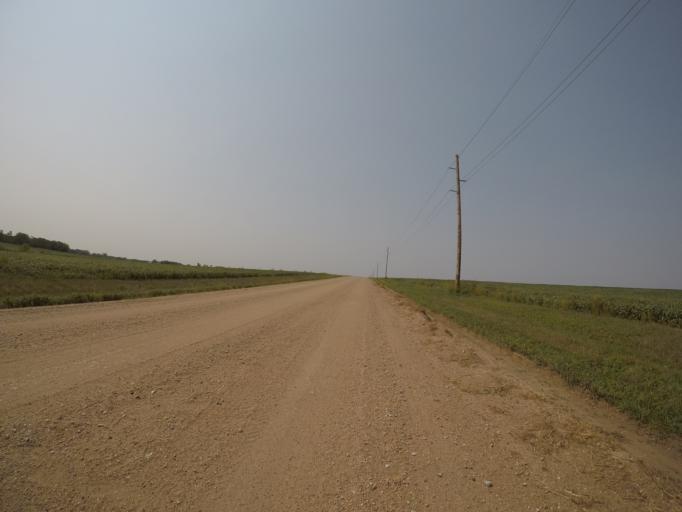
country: US
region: Nebraska
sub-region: Gage County
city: Beatrice
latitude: 40.2774
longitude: -96.8130
